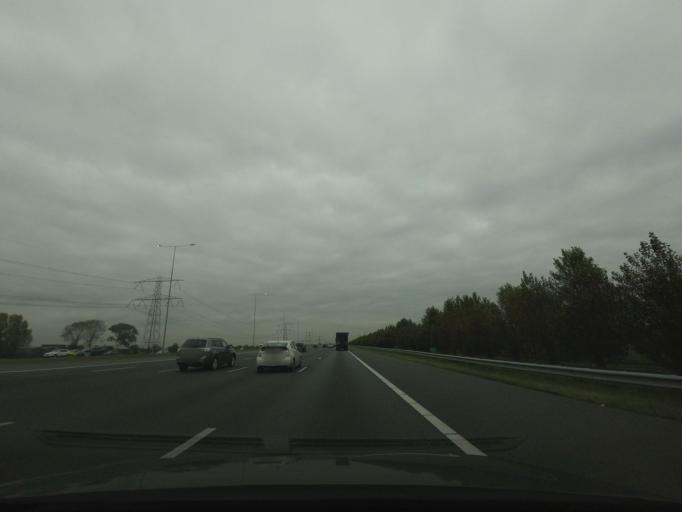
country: NL
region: Utrecht
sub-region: Stichtse Vecht
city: Breukelen
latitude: 52.1973
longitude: 4.9871
